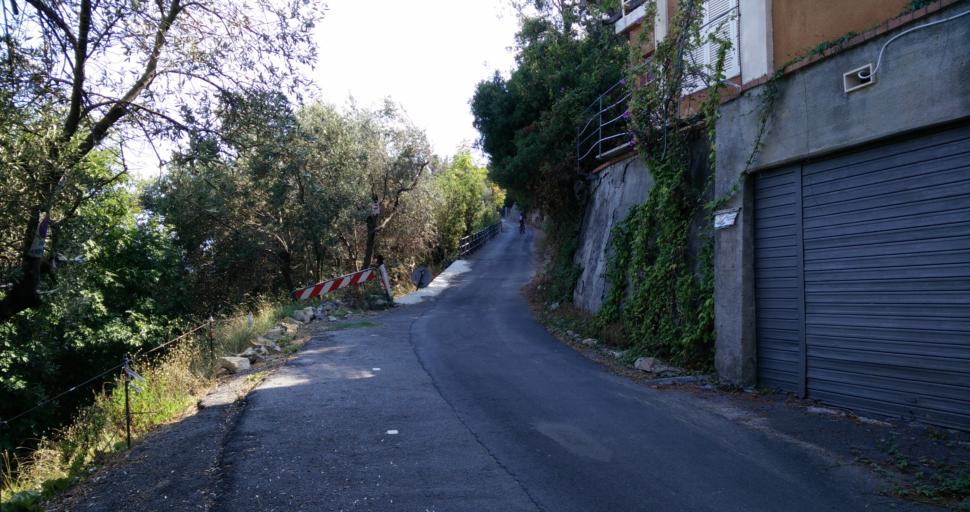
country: IT
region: Liguria
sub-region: Provincia di Savona
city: Alassio
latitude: 43.9975
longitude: 8.1636
